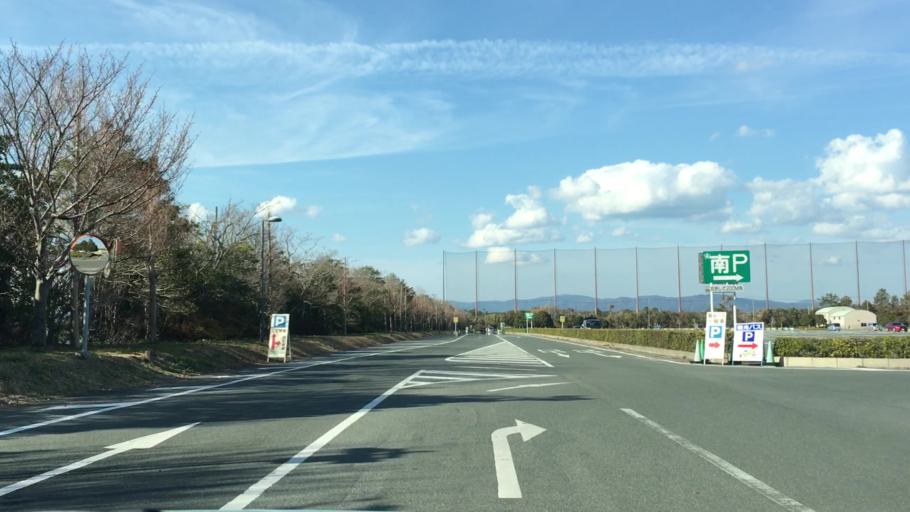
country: JP
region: Shizuoka
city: Kosai-shi
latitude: 34.7130
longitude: 137.5936
